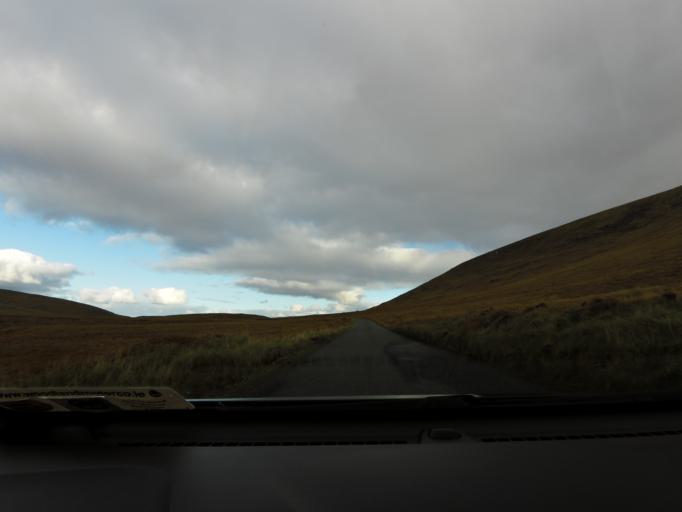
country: IE
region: Connaught
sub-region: Maigh Eo
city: Belmullet
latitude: 53.9315
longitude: -10.0038
